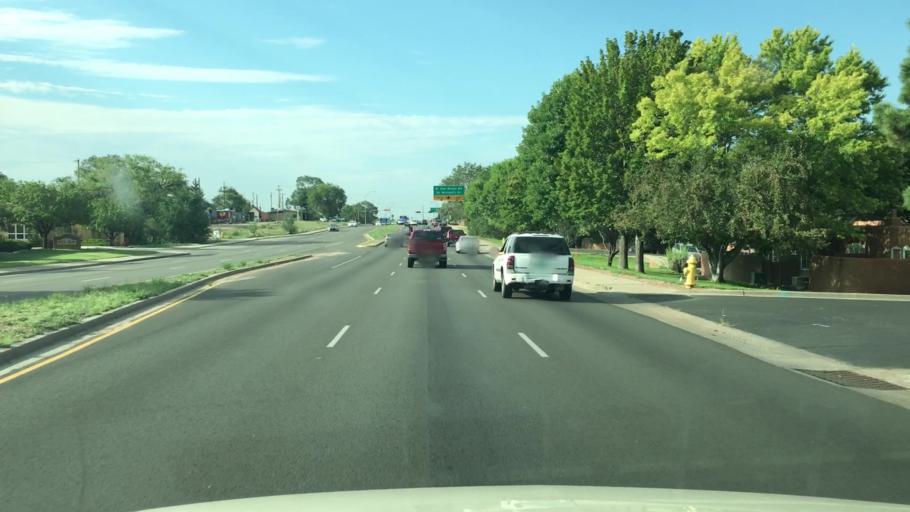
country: US
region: New Mexico
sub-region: Santa Fe County
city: Santa Fe
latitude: 35.6651
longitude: -105.9563
